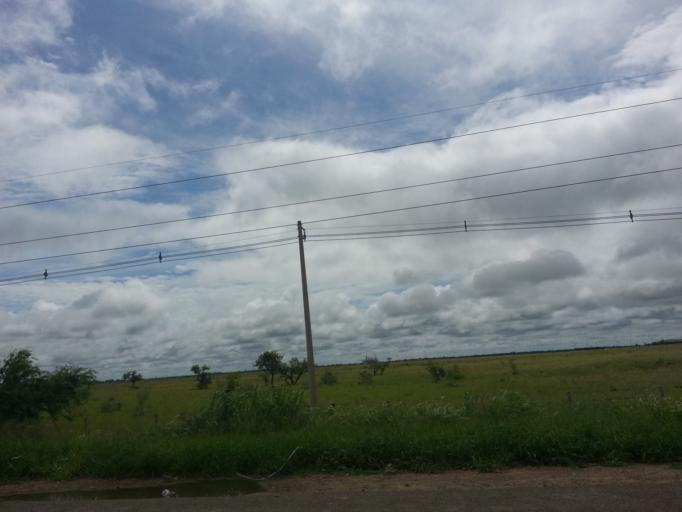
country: BO
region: Santa Cruz
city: La Belgica
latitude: -17.6431
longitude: -63.1575
